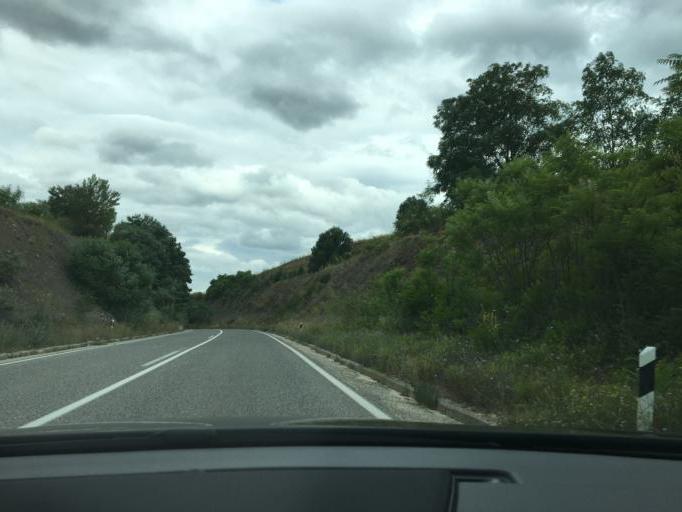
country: MK
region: Opstina Rankovce
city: Rankovce
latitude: 42.1642
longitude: 22.0816
